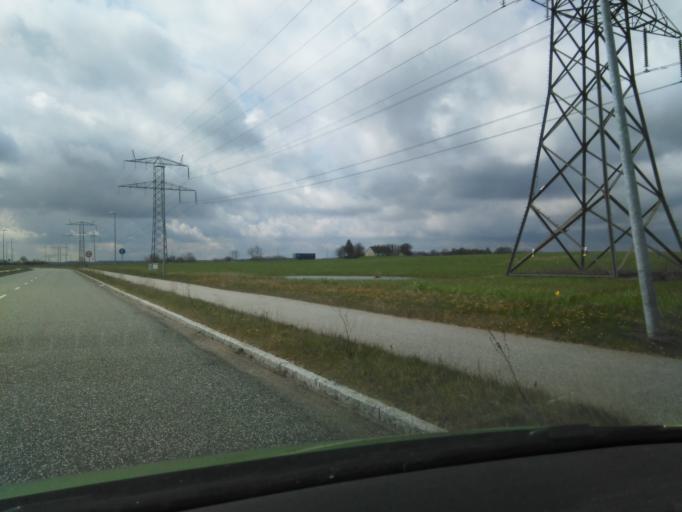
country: DK
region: Central Jutland
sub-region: Arhus Kommune
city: Framlev
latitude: 56.1556
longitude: 10.0588
